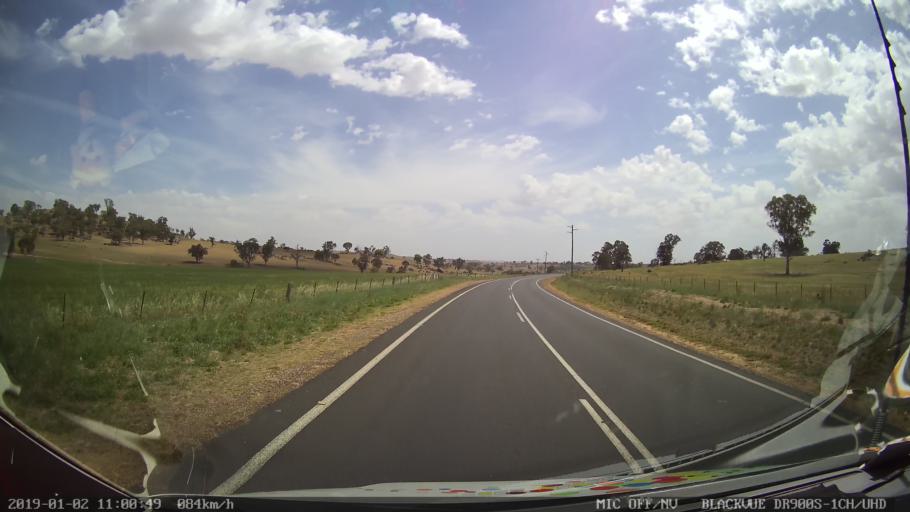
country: AU
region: New South Wales
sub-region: Cootamundra
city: Cootamundra
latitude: -34.6040
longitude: 148.3139
